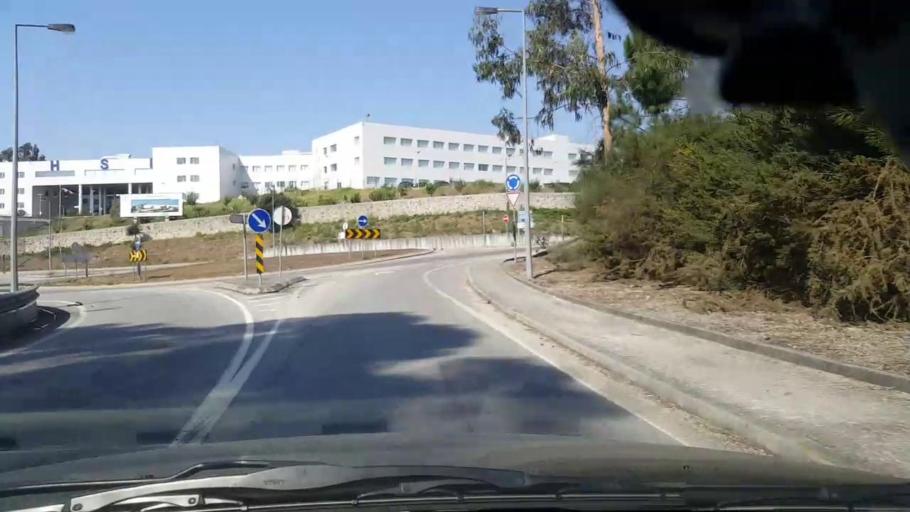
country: PT
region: Porto
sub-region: Vila do Conde
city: Vila do Conde
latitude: 41.3854
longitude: -8.7102
